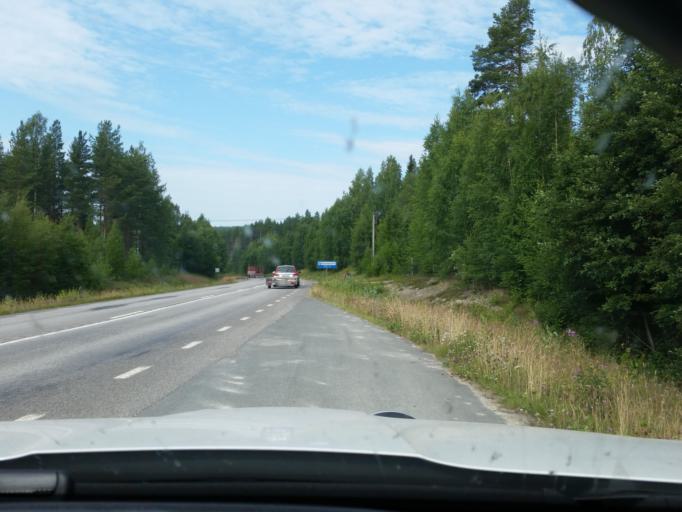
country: SE
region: Norrbotten
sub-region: Alvsbyns Kommun
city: AElvsbyn
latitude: 65.6815
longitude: 20.7989
